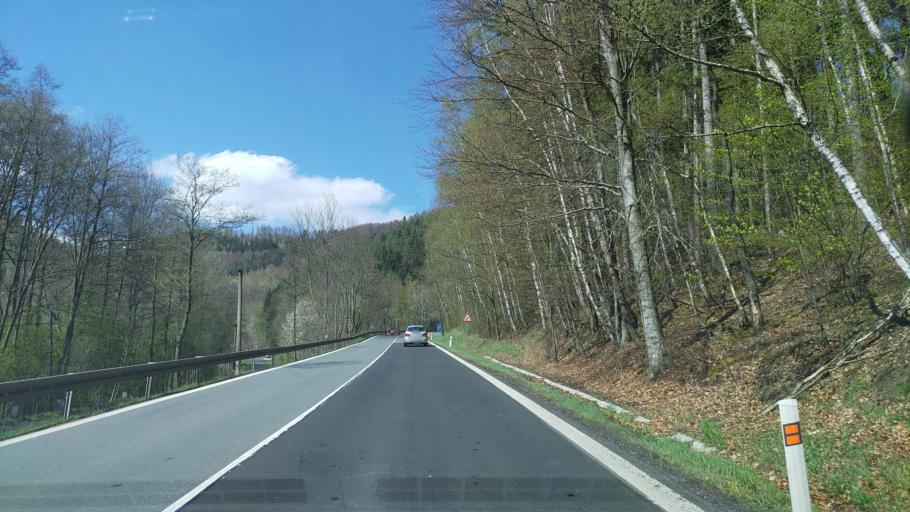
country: CZ
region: Ustecky
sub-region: Okres Chomutov
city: Perstejn
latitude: 50.3700
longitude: 13.0879
